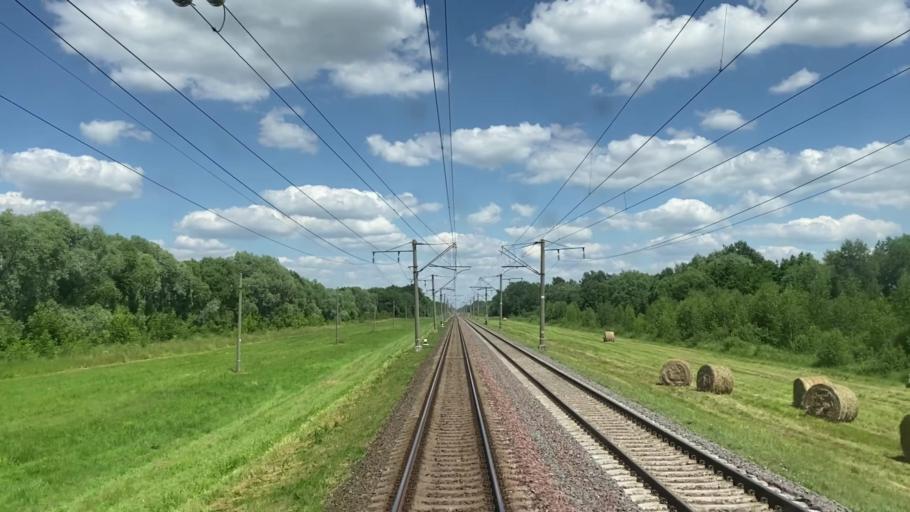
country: BY
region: Brest
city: Zhabinka
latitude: 52.2221
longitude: 24.0648
